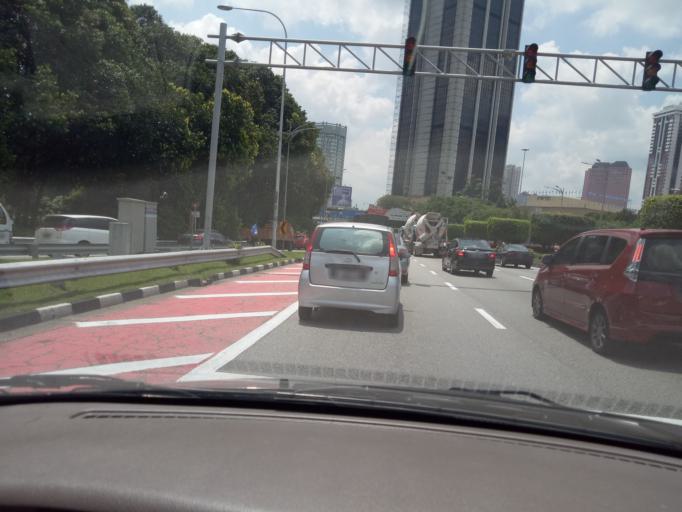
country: MY
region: Kuala Lumpur
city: Kuala Lumpur
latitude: 3.1681
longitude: 101.6888
